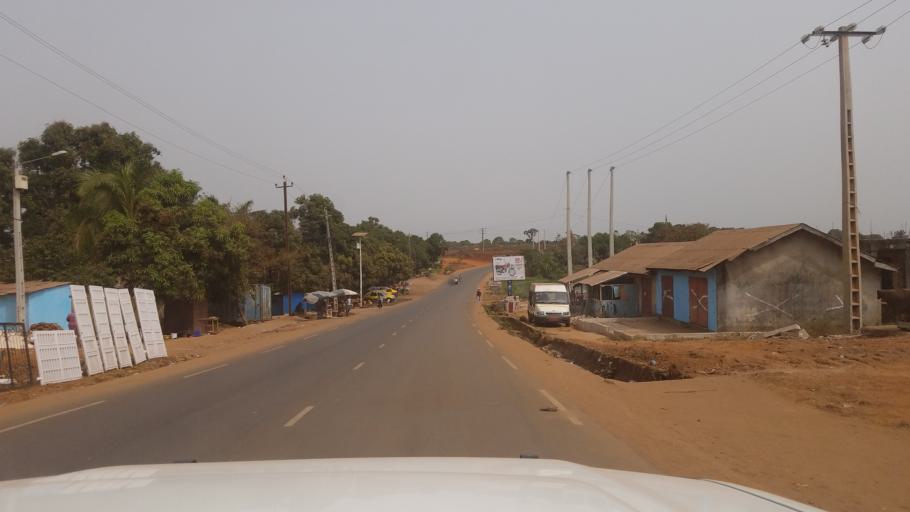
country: GN
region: Kindia
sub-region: Prefecture de Dubreka
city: Dubreka
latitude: 9.6730
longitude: -13.5839
